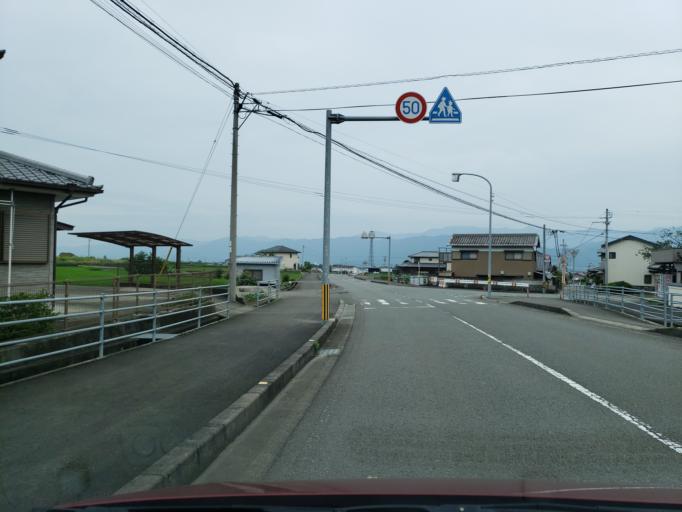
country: JP
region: Tokushima
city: Wakimachi
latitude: 34.0966
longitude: 134.2276
